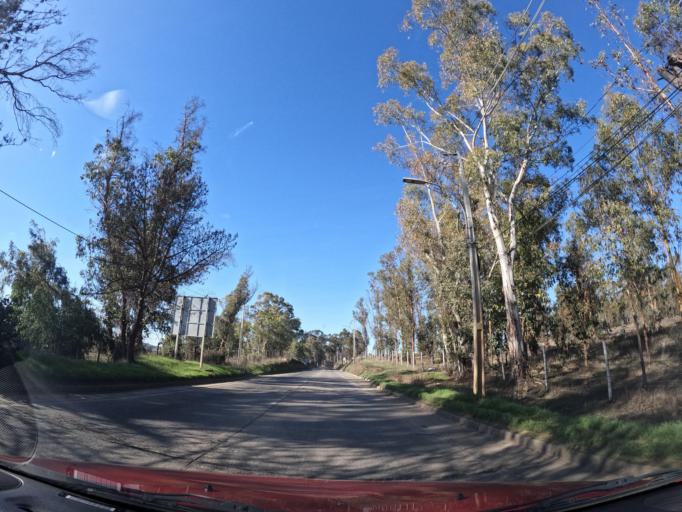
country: CL
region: Maule
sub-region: Provincia de Cauquenes
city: Cauquenes
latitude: -35.9579
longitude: -72.2939
